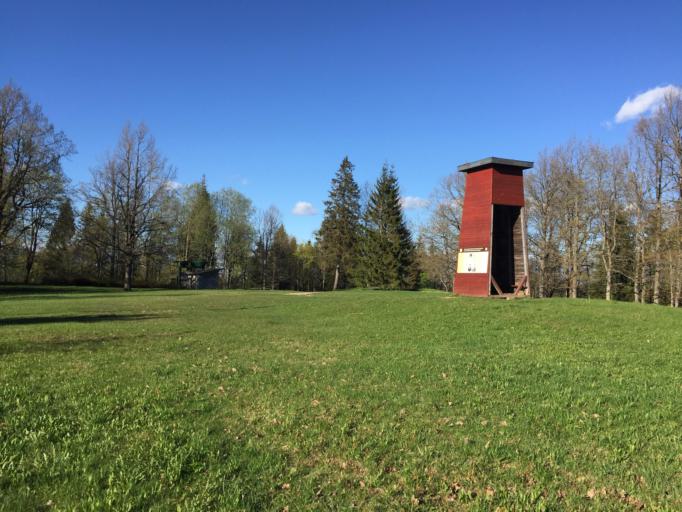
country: LV
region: Vecpiebalga
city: Vecpiebalga
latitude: 56.8699
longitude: 25.9590
